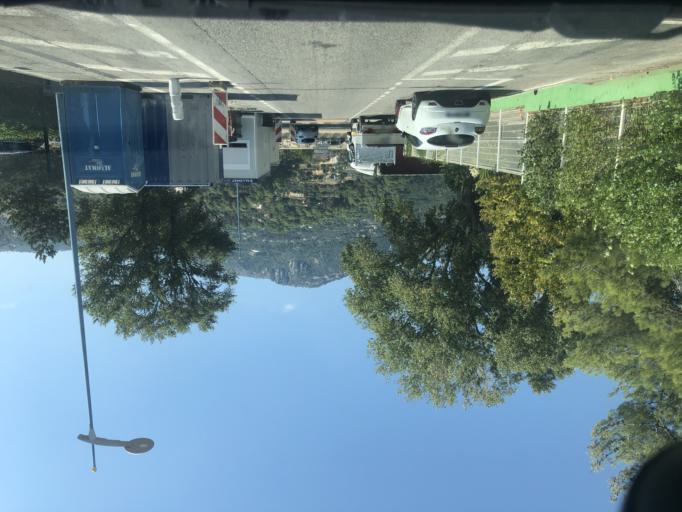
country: FR
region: Provence-Alpes-Cote d'Azur
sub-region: Departement des Alpes-Maritimes
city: Castagniers
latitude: 43.7876
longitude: 7.2112
